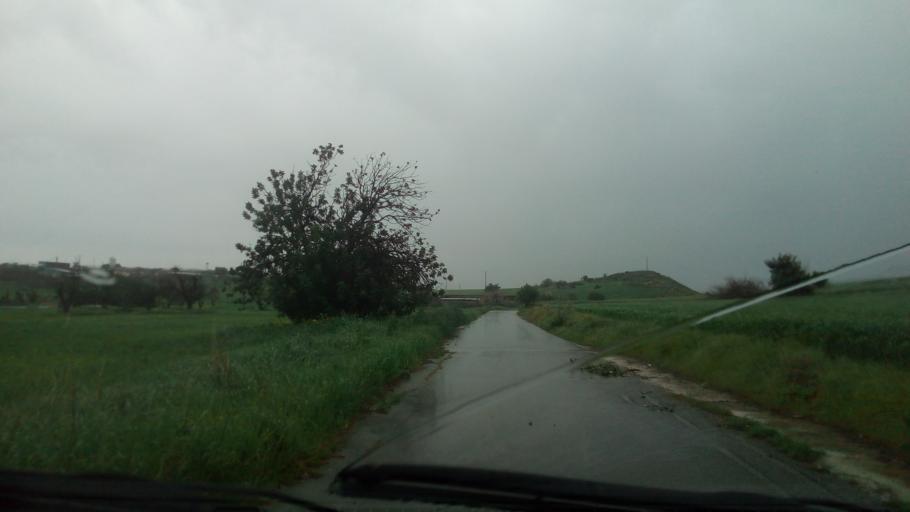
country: CY
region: Larnaka
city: Kofinou
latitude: 34.8468
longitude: 33.4636
